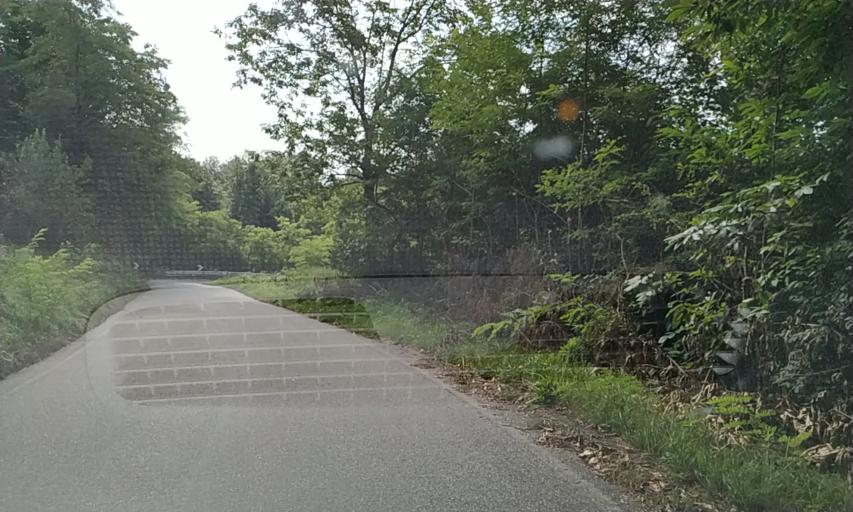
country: IT
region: Piedmont
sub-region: Provincia di Biella
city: Frazione Chiesa
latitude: 45.6901
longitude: 8.2169
